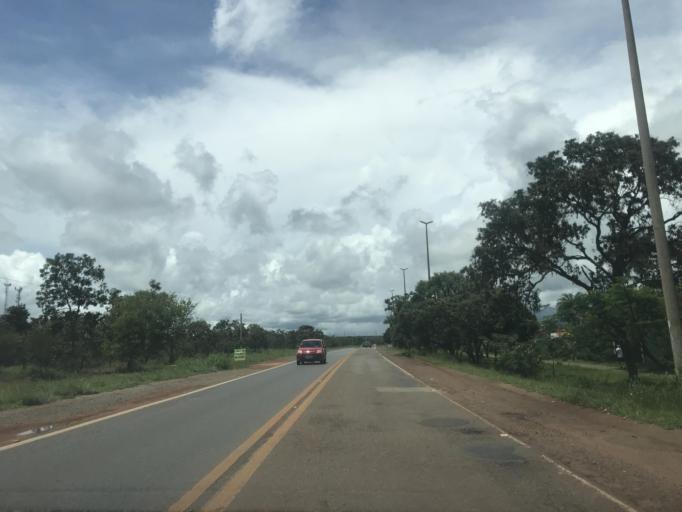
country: BR
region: Federal District
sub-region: Brasilia
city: Brasilia
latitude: -15.6915
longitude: -47.8298
